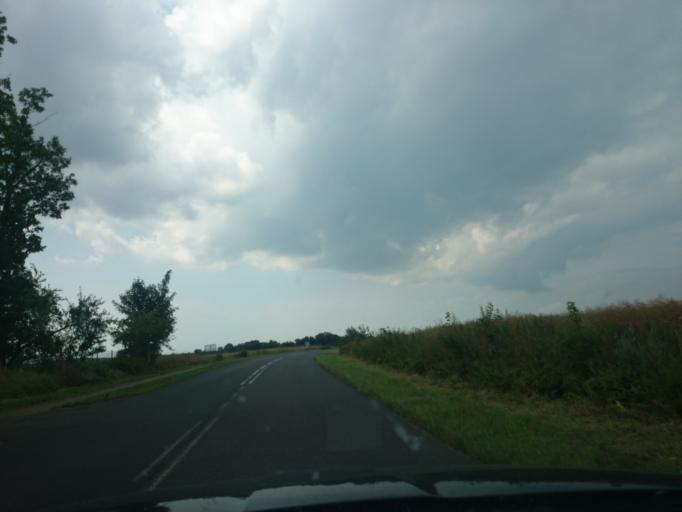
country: PL
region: West Pomeranian Voivodeship
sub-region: Powiat kamienski
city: Wolin
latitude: 53.9239
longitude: 14.6672
